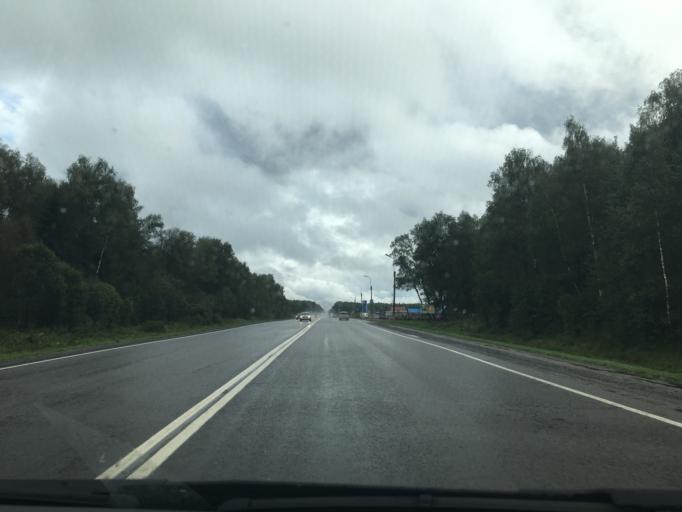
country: RU
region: Kaluga
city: Balabanovo
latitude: 55.1576
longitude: 36.6656
